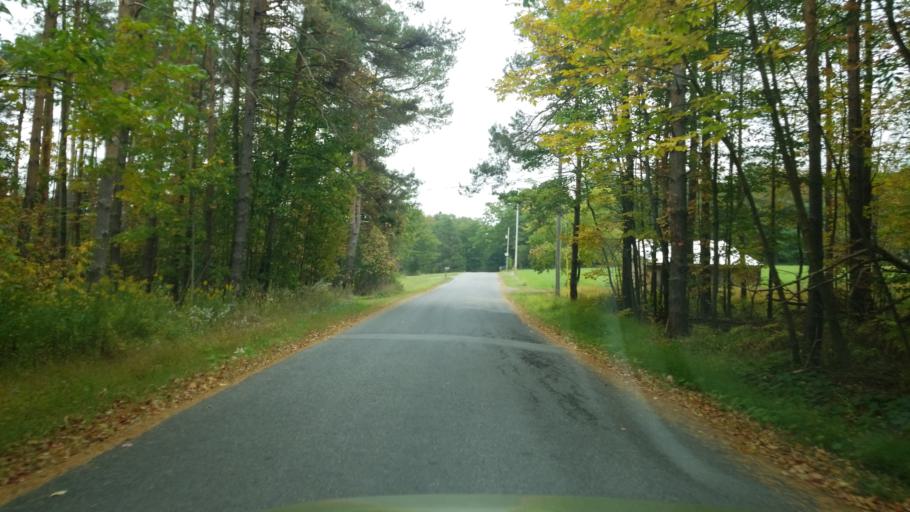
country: US
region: Pennsylvania
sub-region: Clearfield County
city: Curwensville
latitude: 41.0096
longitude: -78.5518
